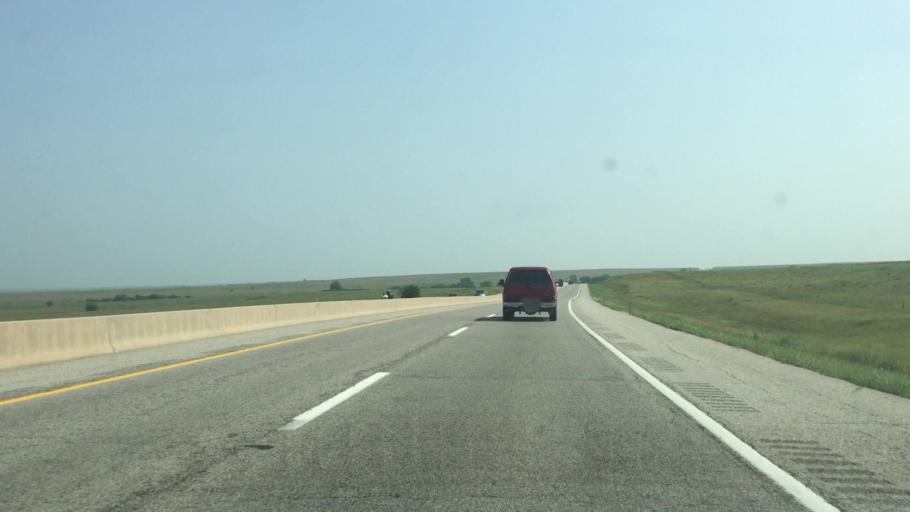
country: US
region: Kansas
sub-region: Lyon County
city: Emporia
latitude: 38.3028
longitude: -96.3479
